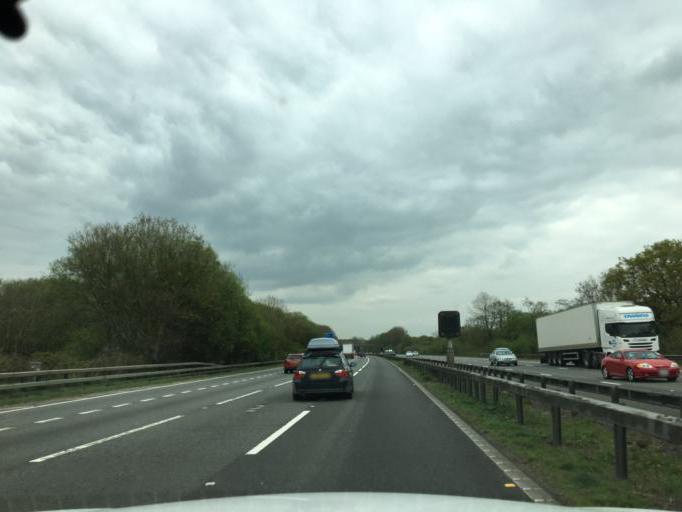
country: GB
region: Wales
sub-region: Rhondda Cynon Taf
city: Llantrisant
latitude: 51.5085
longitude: -3.3451
